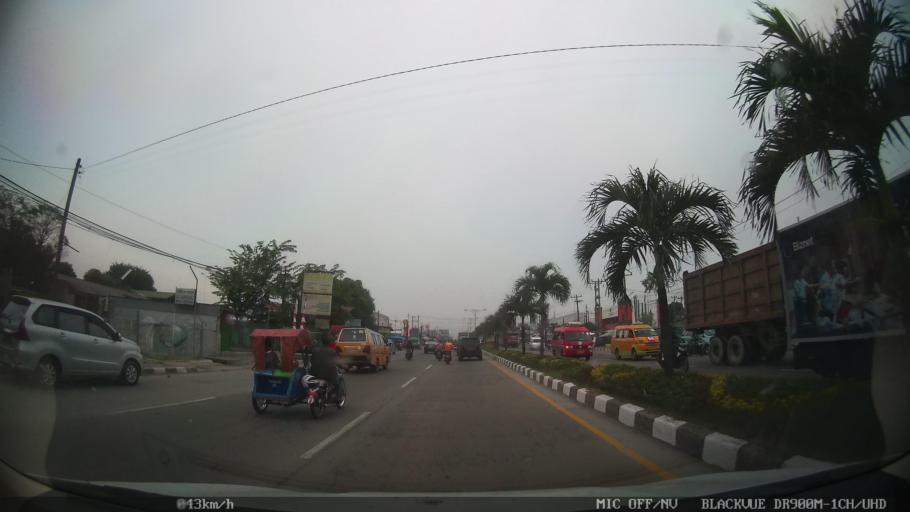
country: ID
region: North Sumatra
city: Deli Tua
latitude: 3.5380
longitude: 98.7071
